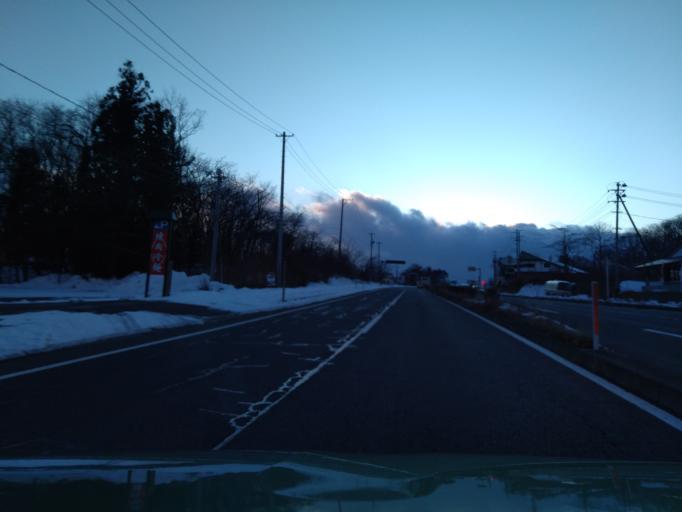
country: JP
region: Iwate
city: Shizukuishi
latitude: 39.7009
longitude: 141.0288
